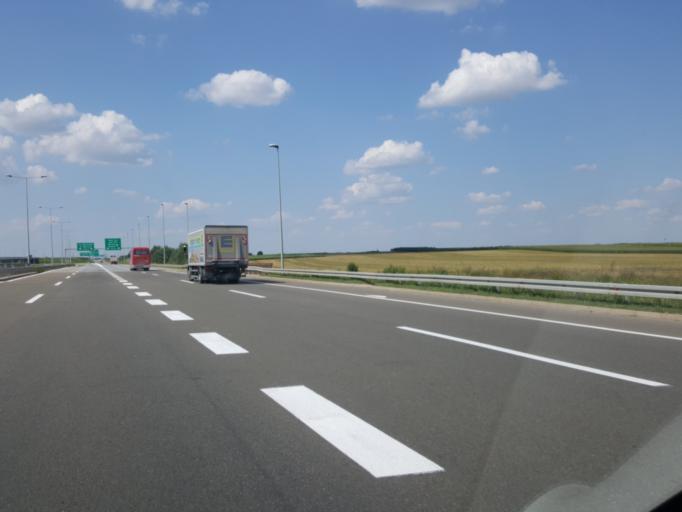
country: RS
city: Dobanovci
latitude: 44.8227
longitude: 20.2523
